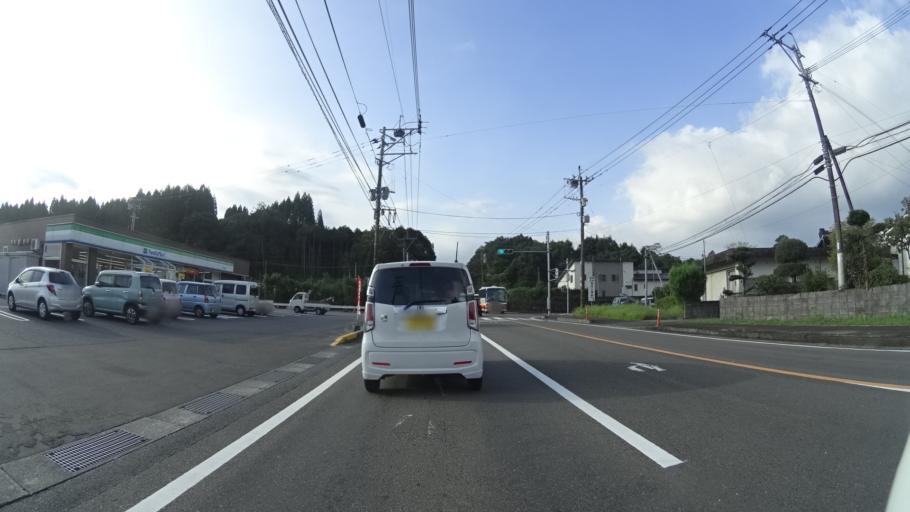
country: JP
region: Kagoshima
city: Okuchi-shinohara
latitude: 32.0406
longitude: 130.5966
